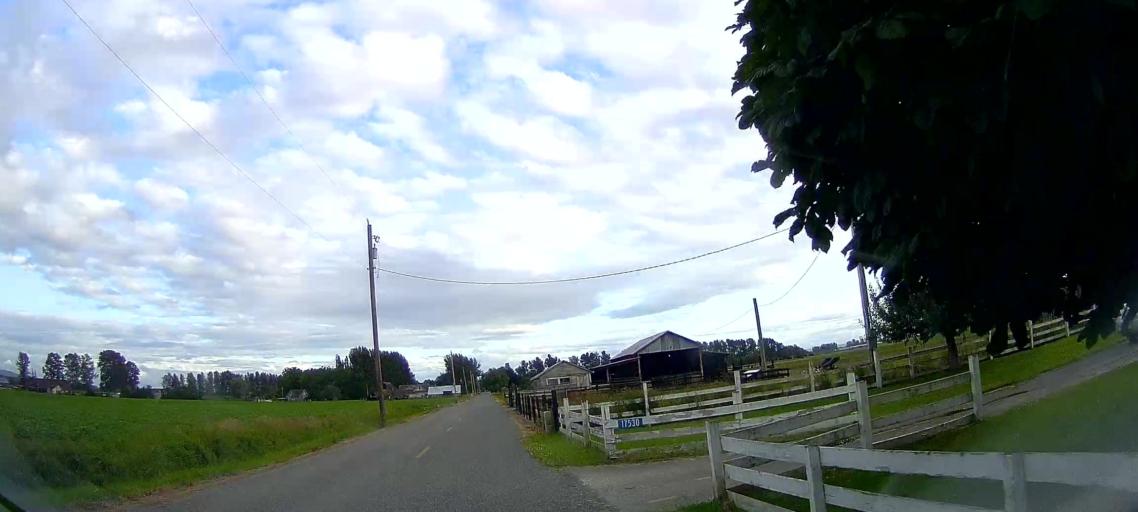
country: US
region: Washington
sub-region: Skagit County
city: Mount Vernon
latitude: 48.3913
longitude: -122.3843
